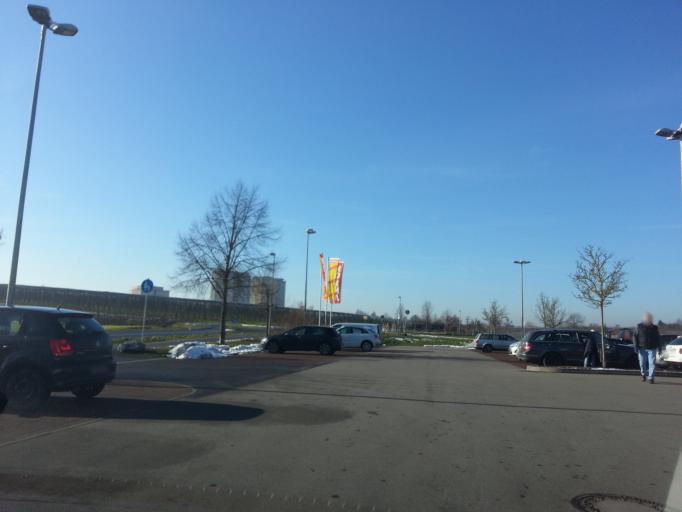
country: DE
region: Baden-Wuerttemberg
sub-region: Tuebingen Region
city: Immenstaad am Bodensee
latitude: 47.6715
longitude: 9.3779
